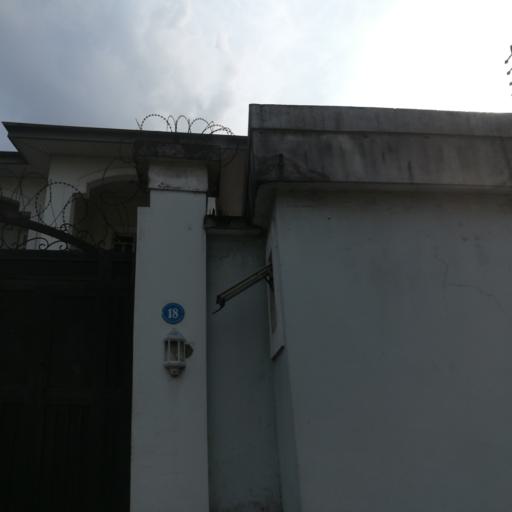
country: NG
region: Rivers
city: Port Harcourt
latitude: 4.8420
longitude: 7.0539
